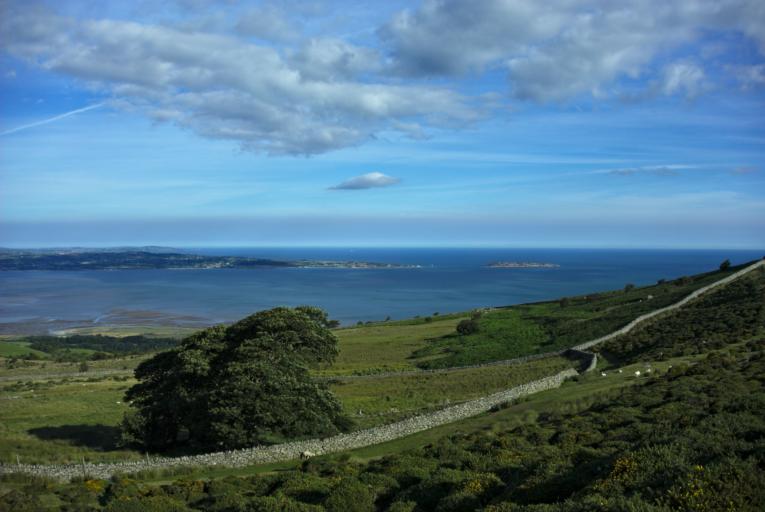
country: GB
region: Wales
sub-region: Conwy
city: Llanfairfechan
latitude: 53.2356
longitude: -3.9660
